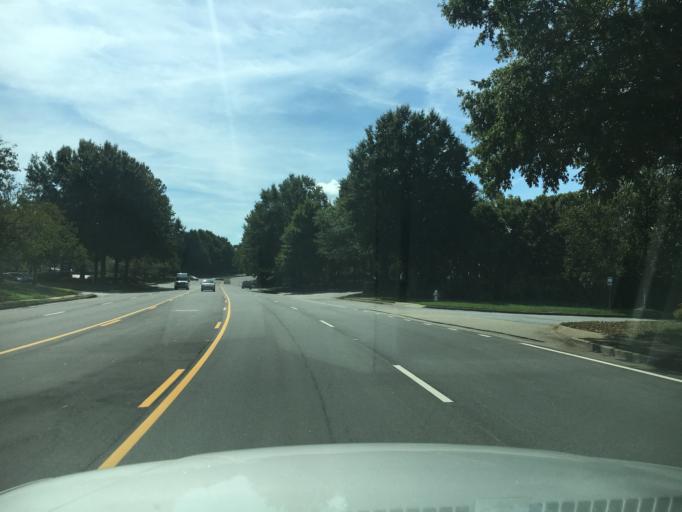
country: US
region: Georgia
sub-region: Gwinnett County
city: Duluth
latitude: 33.9675
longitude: -84.1185
